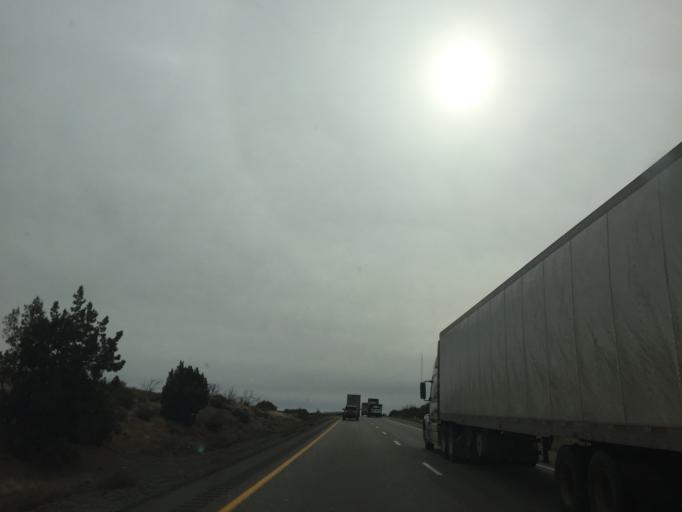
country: US
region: Utah
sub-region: Washington County
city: Toquerville
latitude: 37.3011
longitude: -113.2994
